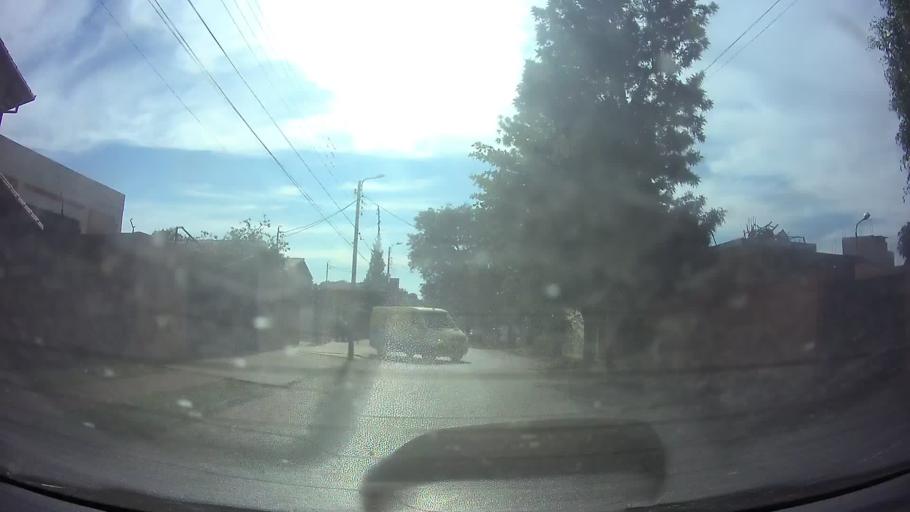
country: PY
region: Central
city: Fernando de la Mora
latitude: -25.3334
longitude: -57.5633
